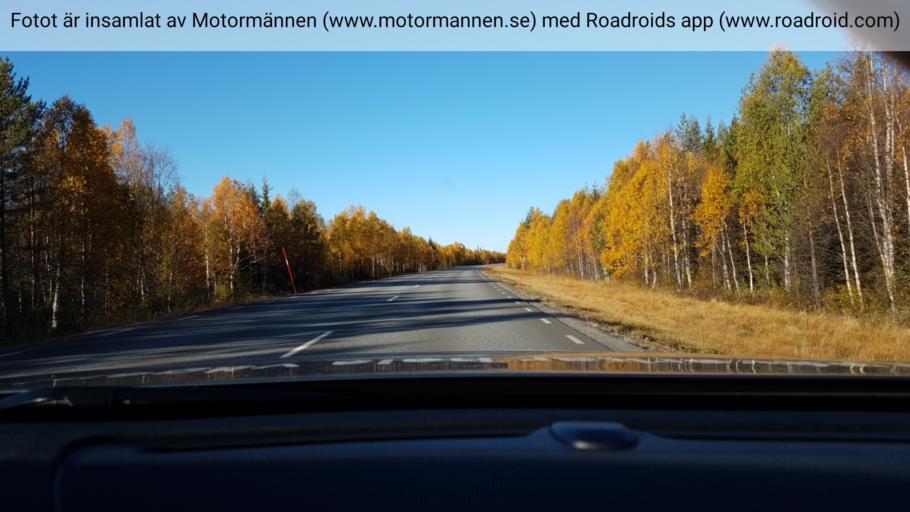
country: SE
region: Norrbotten
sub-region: Arvidsjaurs Kommun
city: Arvidsjaur
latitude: 65.4335
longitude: 19.5115
